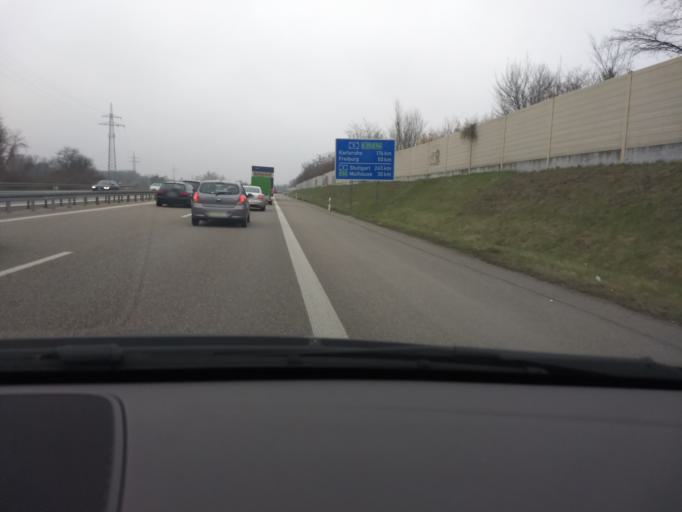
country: FR
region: Alsace
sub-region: Departement du Haut-Rhin
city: Kembs
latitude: 47.6852
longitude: 7.5220
